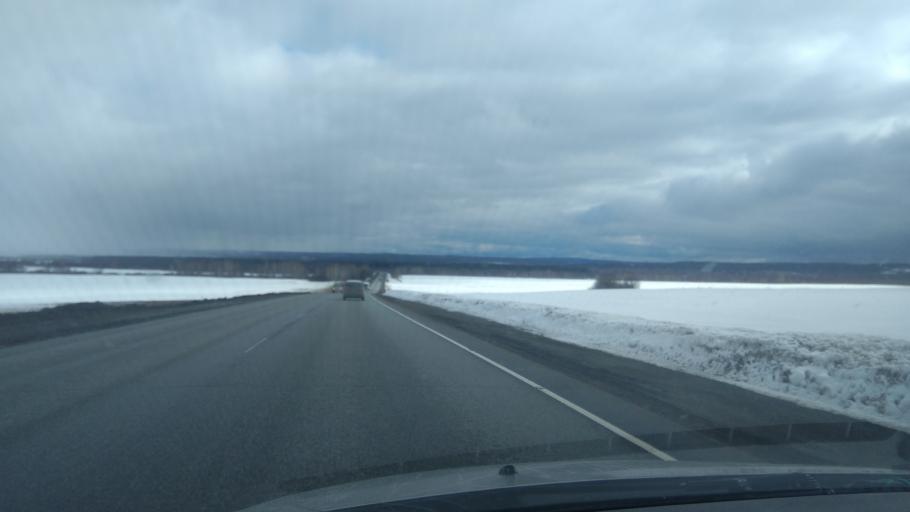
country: RU
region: Sverdlovsk
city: Ufimskiy
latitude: 56.7735
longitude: 58.0621
